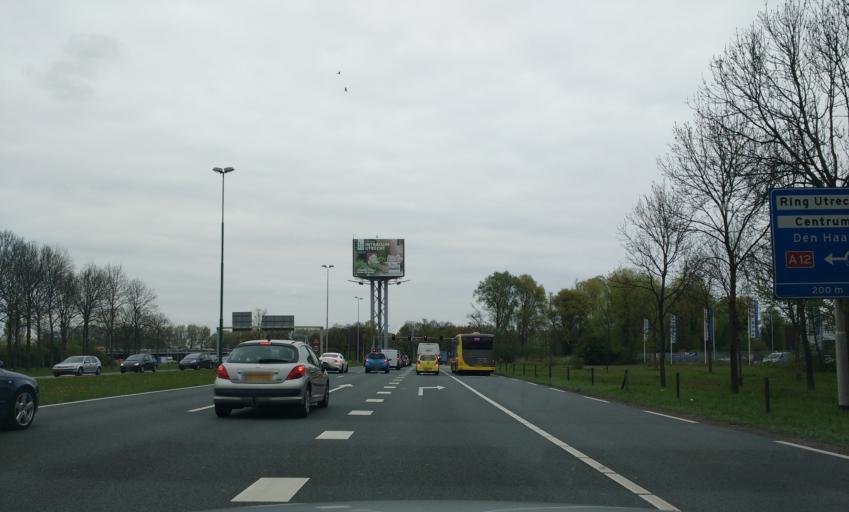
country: NL
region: Utrecht
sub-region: Gemeente Utrecht
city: Lunetten
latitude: 52.0533
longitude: 5.1210
